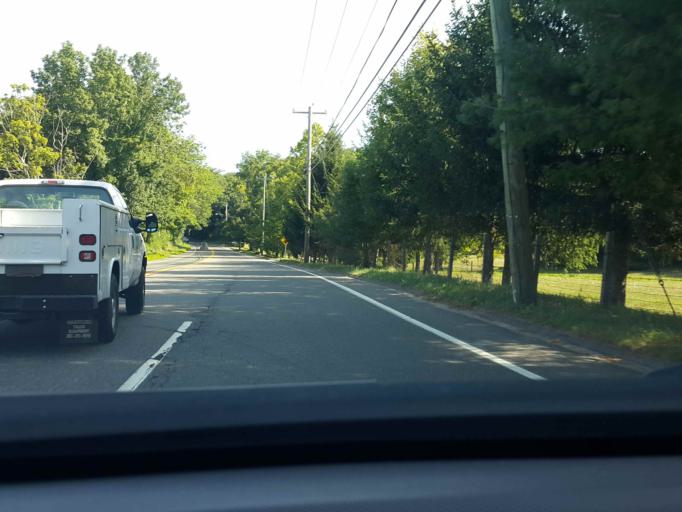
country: US
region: Connecticut
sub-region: New Haven County
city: Guilford
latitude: 41.2992
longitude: -72.6874
